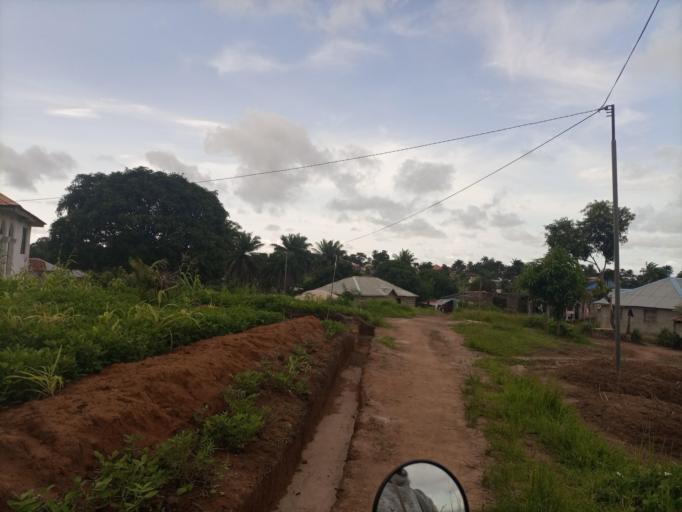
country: SL
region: Northern Province
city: Masoyila
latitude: 8.6049
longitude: -13.1709
